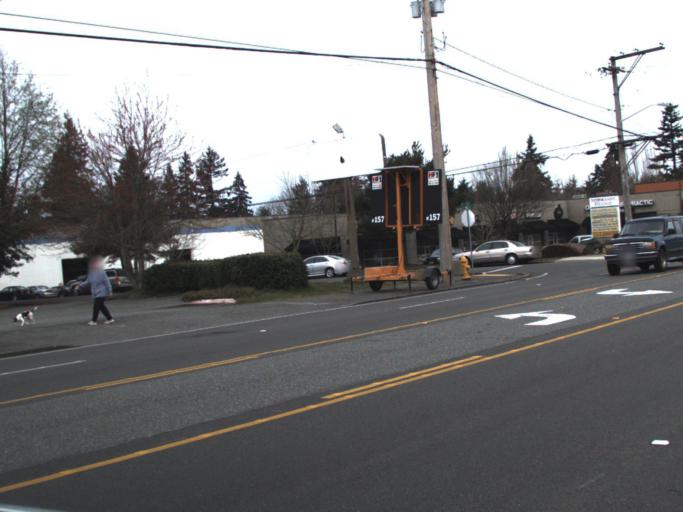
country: US
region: Washington
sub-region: King County
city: Normandy Park
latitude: 47.4431
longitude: -122.3342
